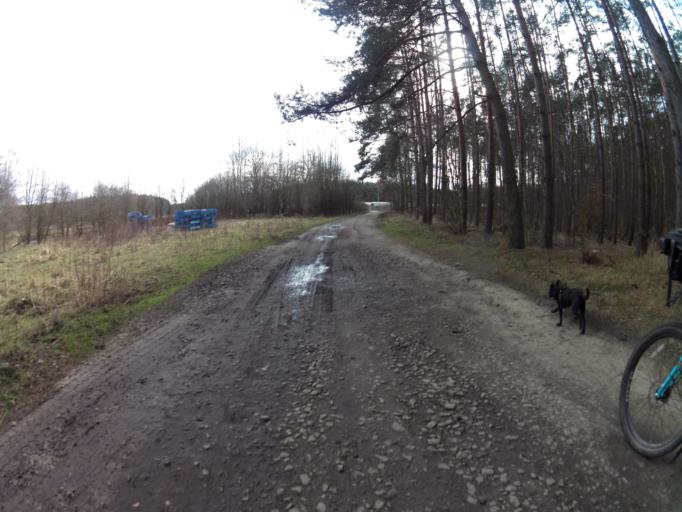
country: PL
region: Lubusz
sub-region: Powiat gorzowski
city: Lubiszyn
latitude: 52.7709
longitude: 14.8384
